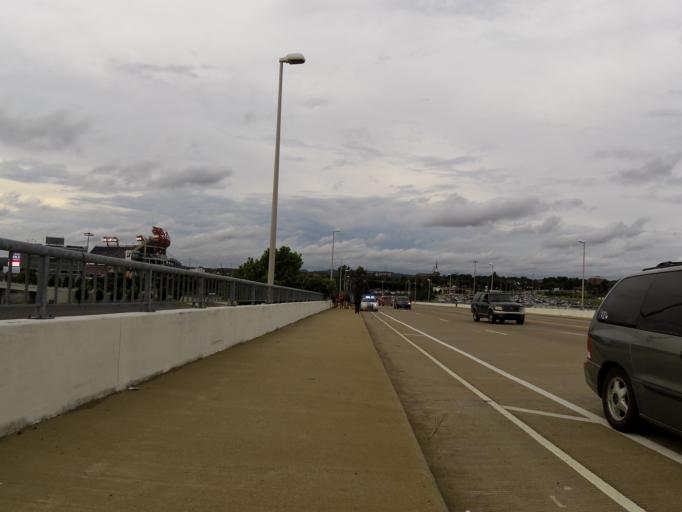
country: US
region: Tennessee
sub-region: Davidson County
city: Nashville
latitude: 36.1618
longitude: -86.7691
